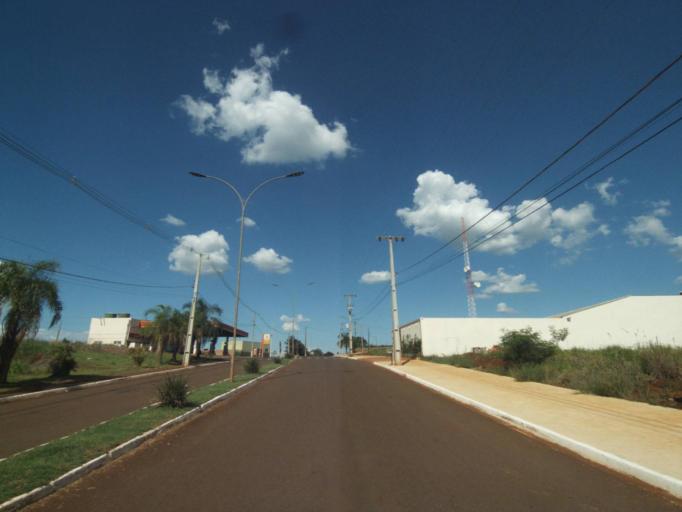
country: BR
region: Parana
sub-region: Sertanopolis
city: Sertanopolis
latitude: -23.0391
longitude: -50.8108
